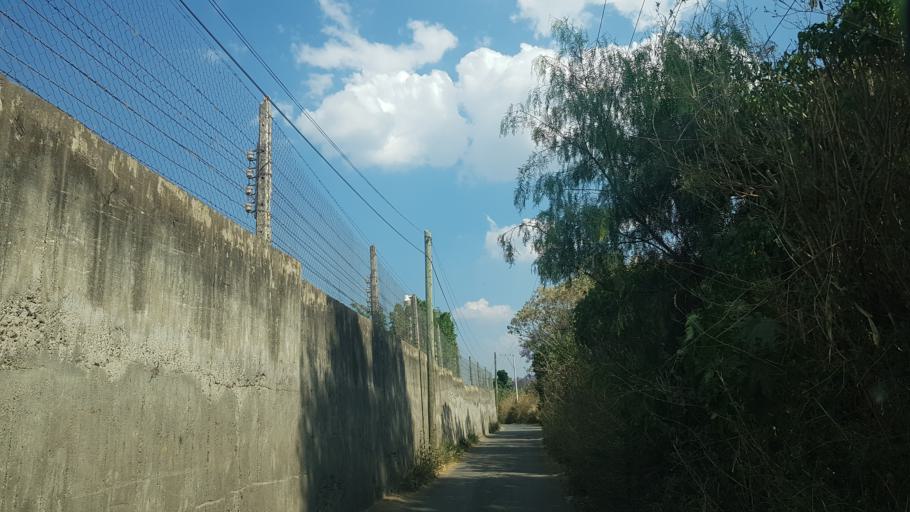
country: MX
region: Puebla
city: Atlixco
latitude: 18.8739
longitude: -98.4859
